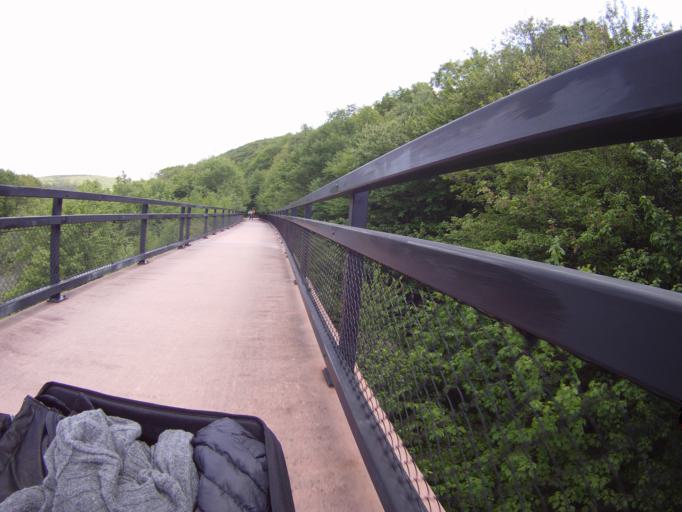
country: US
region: Pennsylvania
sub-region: Somerset County
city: Meyersdale
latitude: 39.8097
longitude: -78.9949
